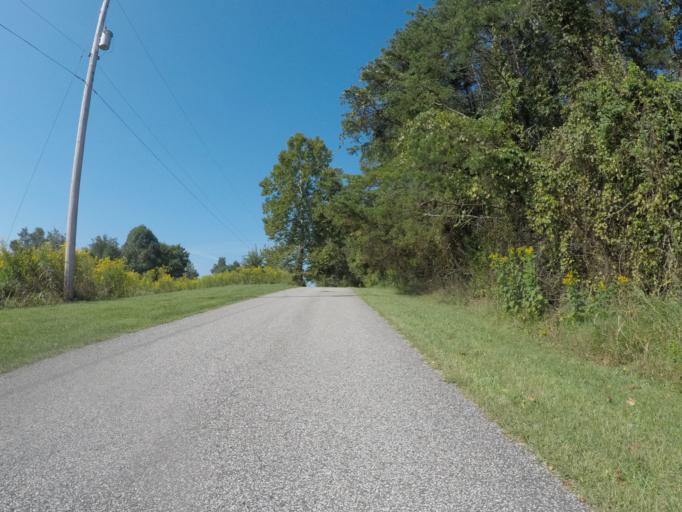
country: US
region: West Virginia
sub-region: Cabell County
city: Barboursville
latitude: 38.3653
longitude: -82.2713
